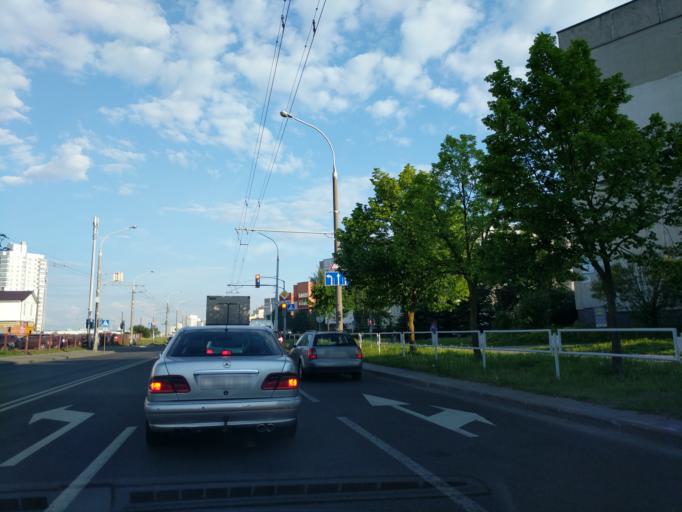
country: BY
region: Minsk
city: Novoye Medvezhino
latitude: 53.8896
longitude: 27.4413
